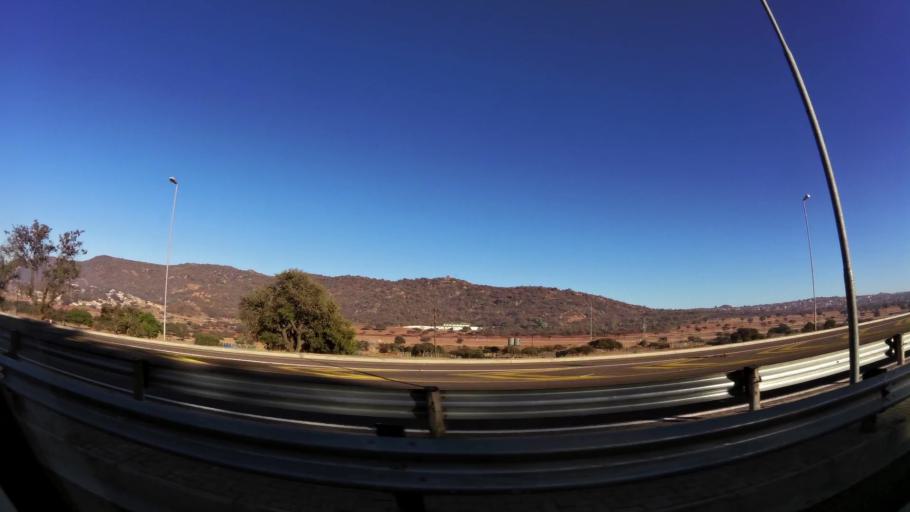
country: ZA
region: Limpopo
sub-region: Capricorn District Municipality
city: Mankoeng
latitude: -23.9311
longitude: 29.7953
